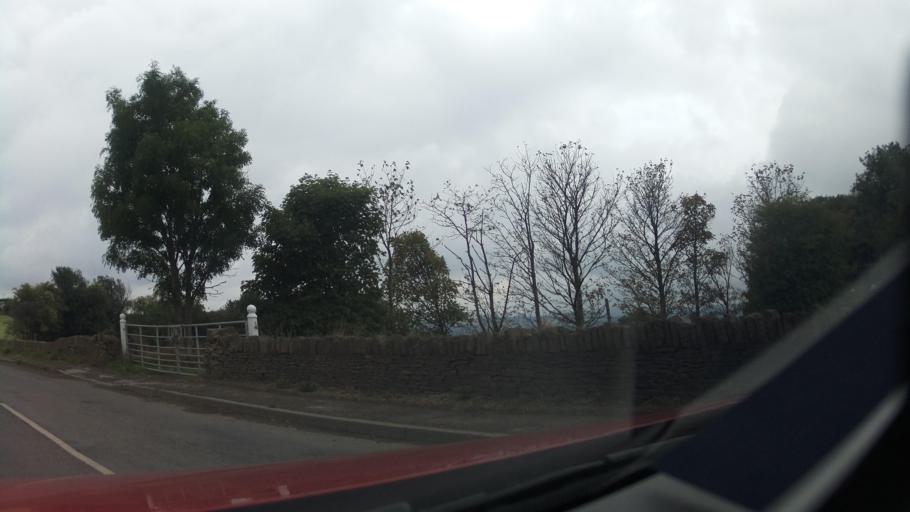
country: GB
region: England
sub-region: Kirklees
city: Shelley
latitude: 53.6102
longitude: -1.6730
